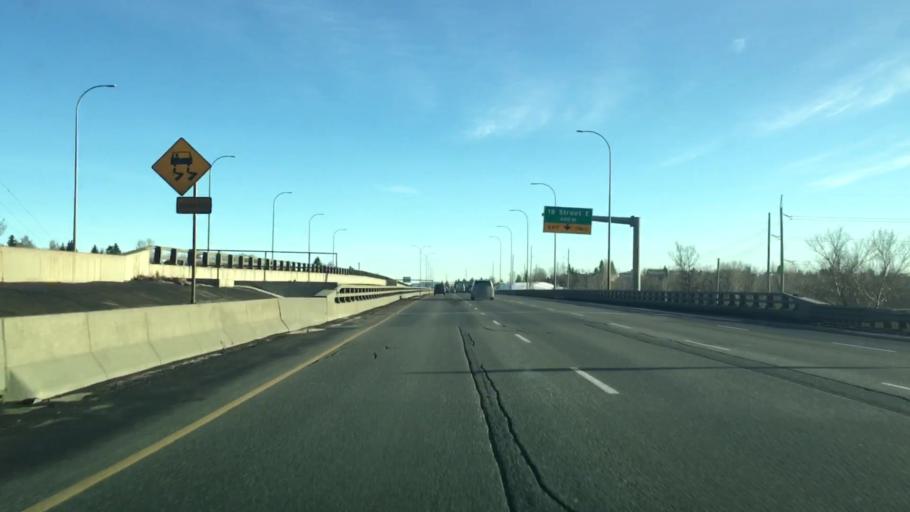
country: CA
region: Alberta
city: Calgary
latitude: 50.9878
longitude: -114.0263
